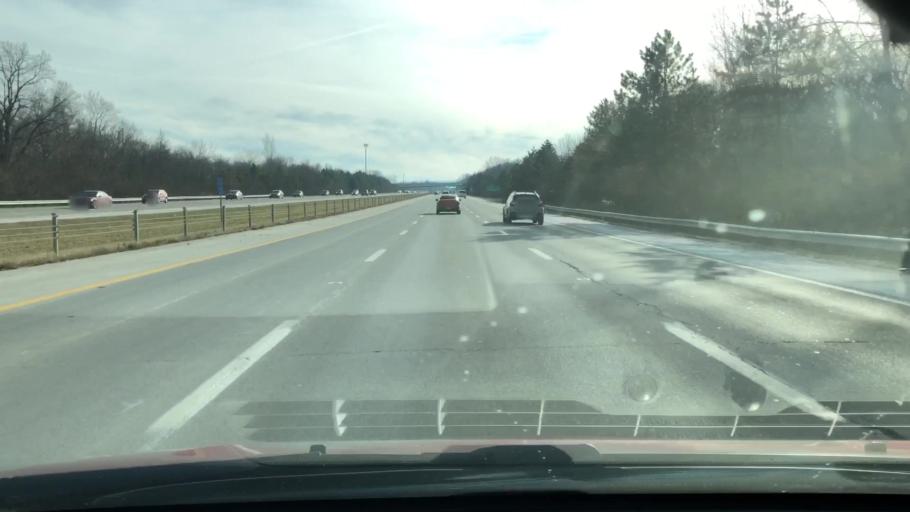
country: US
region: Ohio
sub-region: Greene County
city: Beavercreek
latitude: 39.7223
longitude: -84.0913
